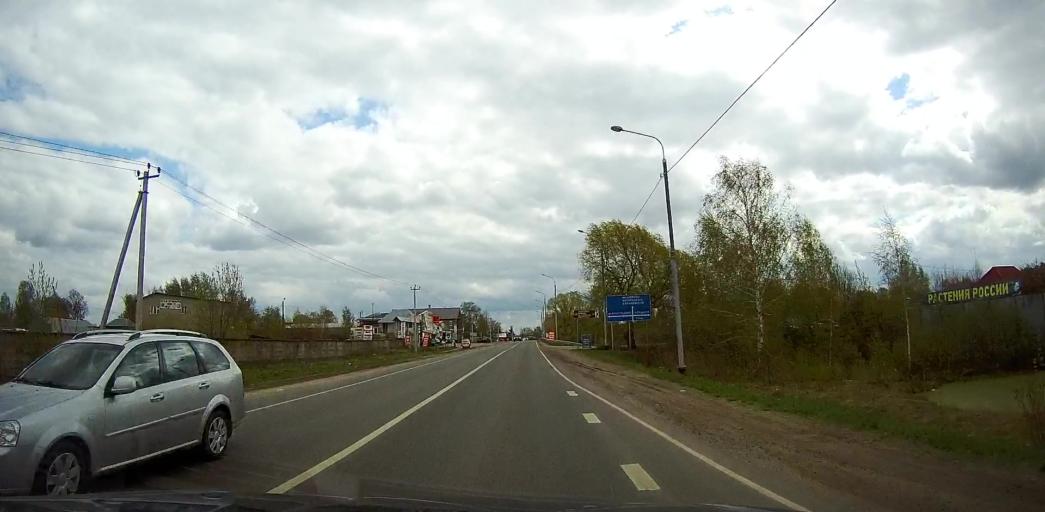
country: RU
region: Moskovskaya
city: Ashitkovo
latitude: 55.4271
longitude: 38.5509
